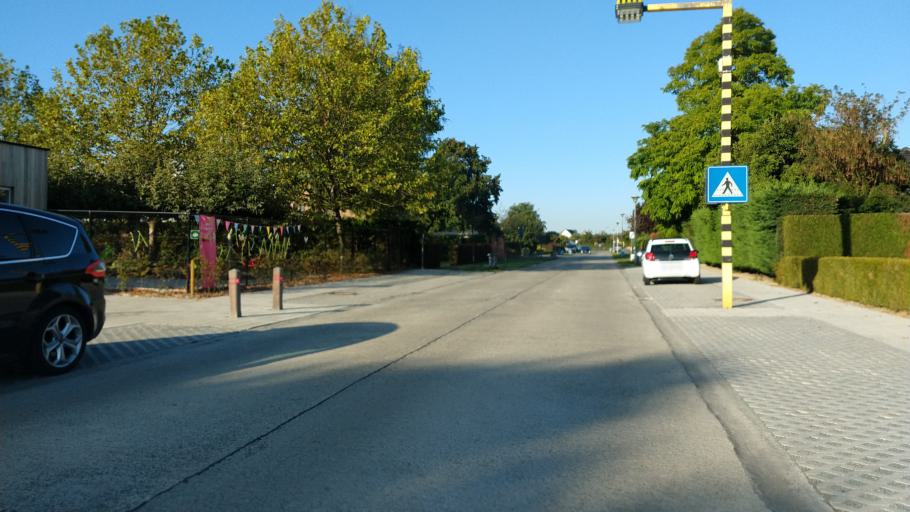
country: BE
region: Flanders
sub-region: Provincie Oost-Vlaanderen
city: Lochristi
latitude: 51.0882
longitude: 3.8523
